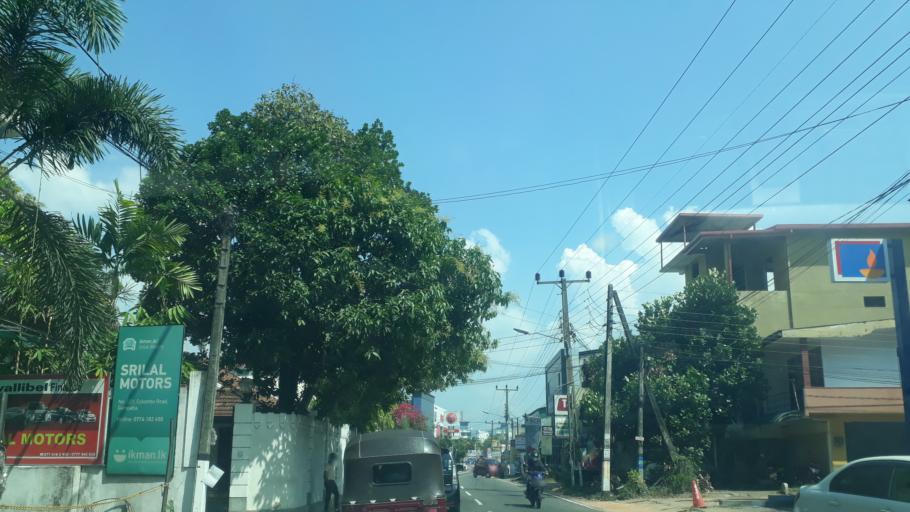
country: LK
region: Western
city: Gampaha
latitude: 7.0902
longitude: 80.0026
